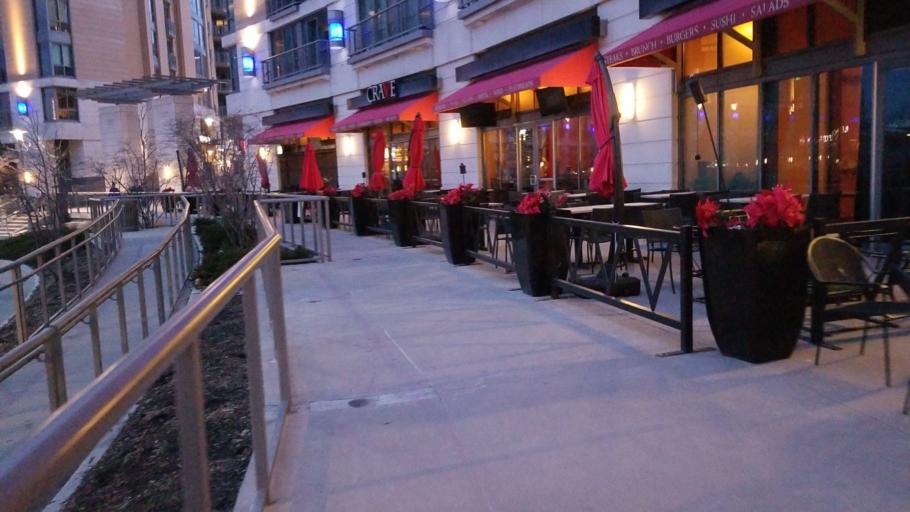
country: US
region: Nebraska
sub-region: Douglas County
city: Omaha
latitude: 41.2587
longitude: -95.9604
